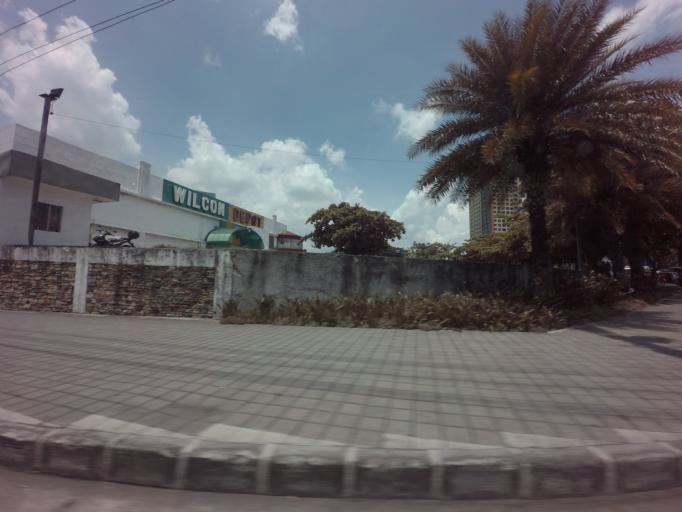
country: PH
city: Sambayanihan People's Village
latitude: 14.4223
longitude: 121.0398
